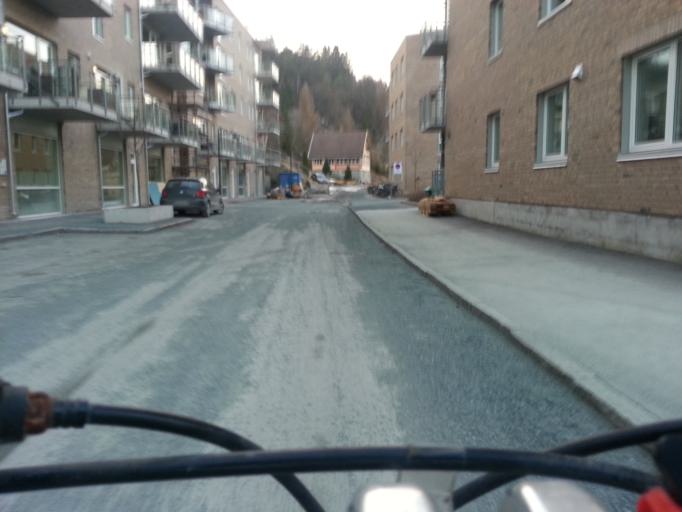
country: NO
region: Sor-Trondelag
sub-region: Trondheim
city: Trondheim
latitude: 63.4328
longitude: 10.3523
